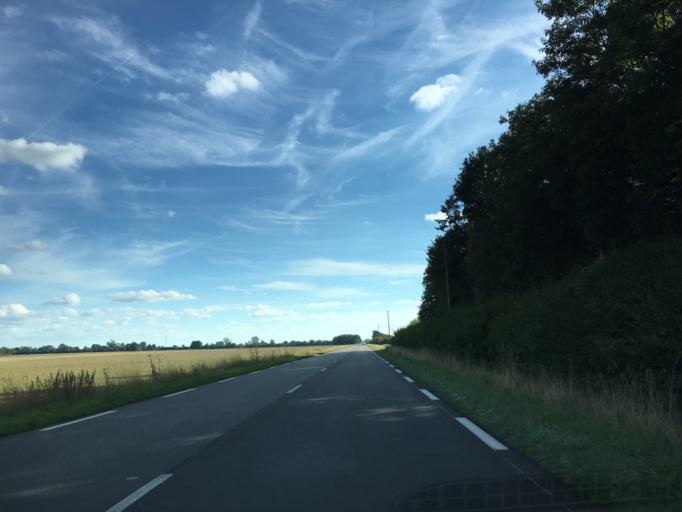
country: FR
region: Lower Normandy
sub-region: Departement du Calvados
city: Orbec
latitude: 48.9400
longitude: 0.4498
